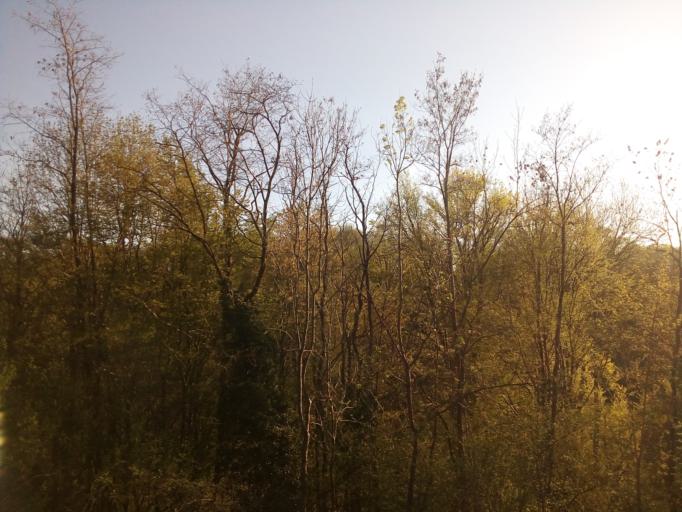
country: FR
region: Rhone-Alpes
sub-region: Departement de l'Isere
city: Saint-Didier-de-la-Tour
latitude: 45.5575
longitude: 5.5010
